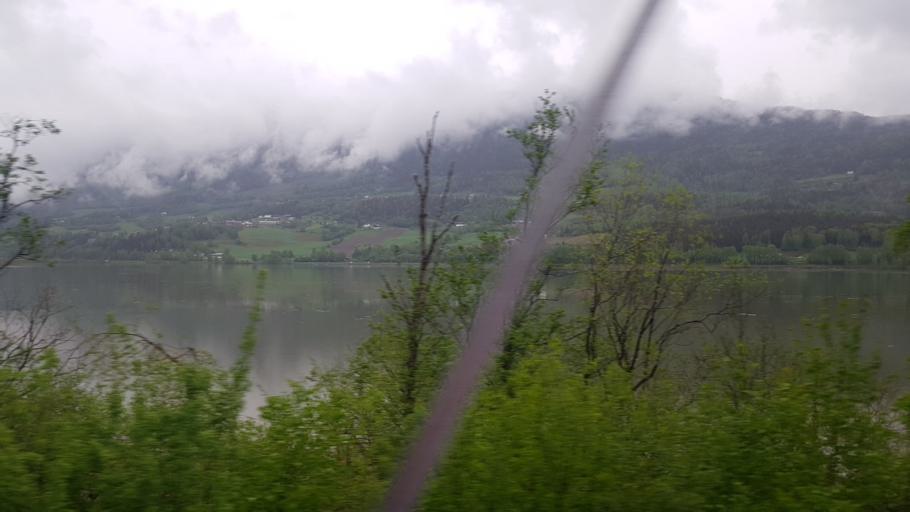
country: NO
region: Oppland
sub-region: Ringebu
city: Ringebu
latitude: 61.4477
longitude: 10.2096
